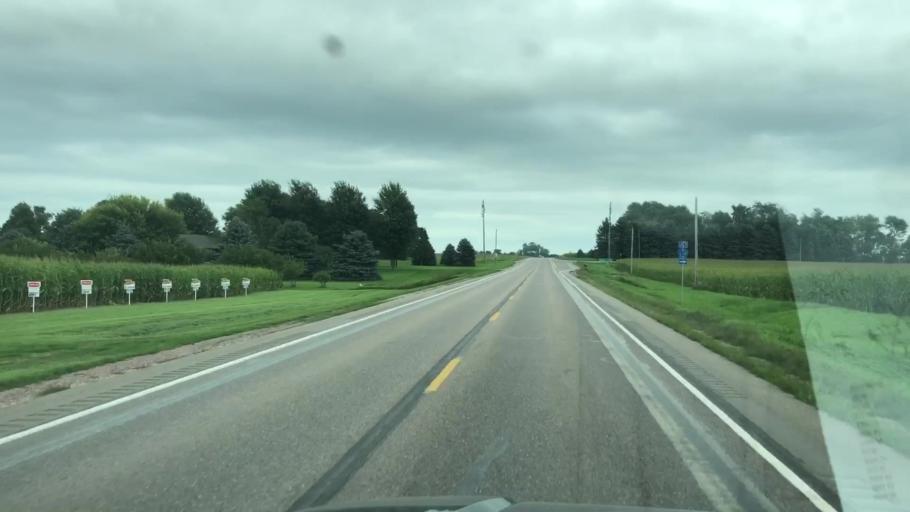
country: US
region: Iowa
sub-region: O'Brien County
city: Sheldon
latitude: 43.1863
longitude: -95.9830
